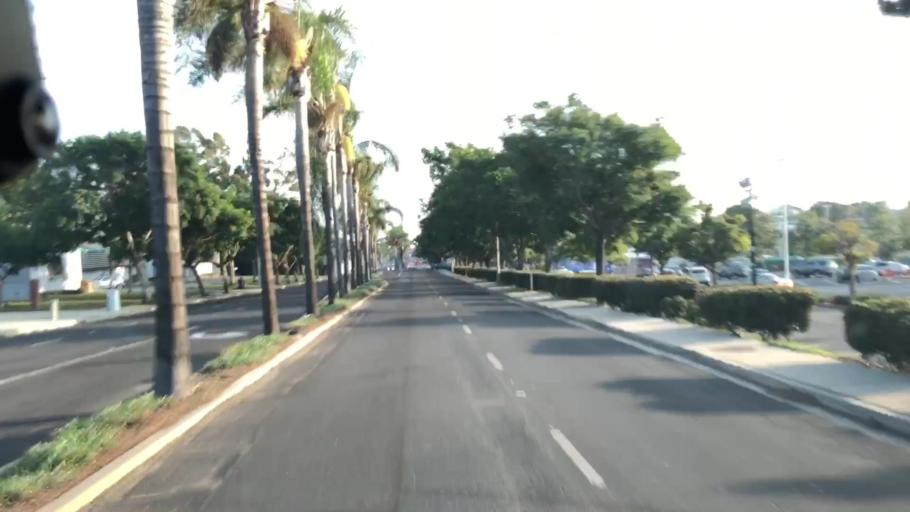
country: US
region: California
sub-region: Ventura County
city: Ventura
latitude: 34.2723
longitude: -119.2476
